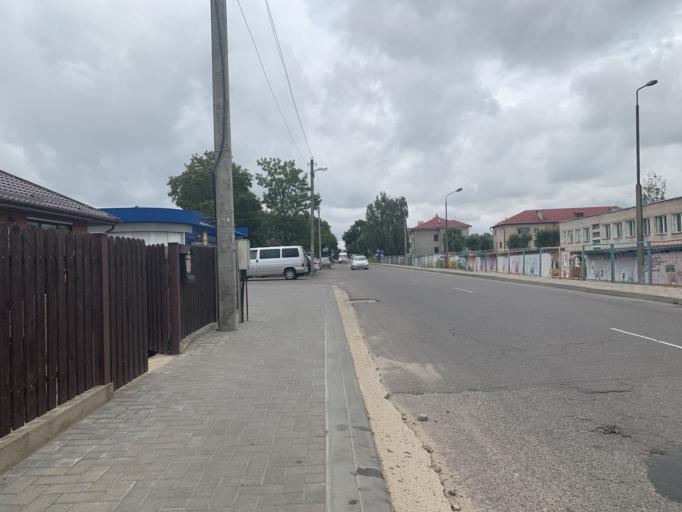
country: BY
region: Minsk
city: Nyasvizh
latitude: 53.2213
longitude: 26.6708
